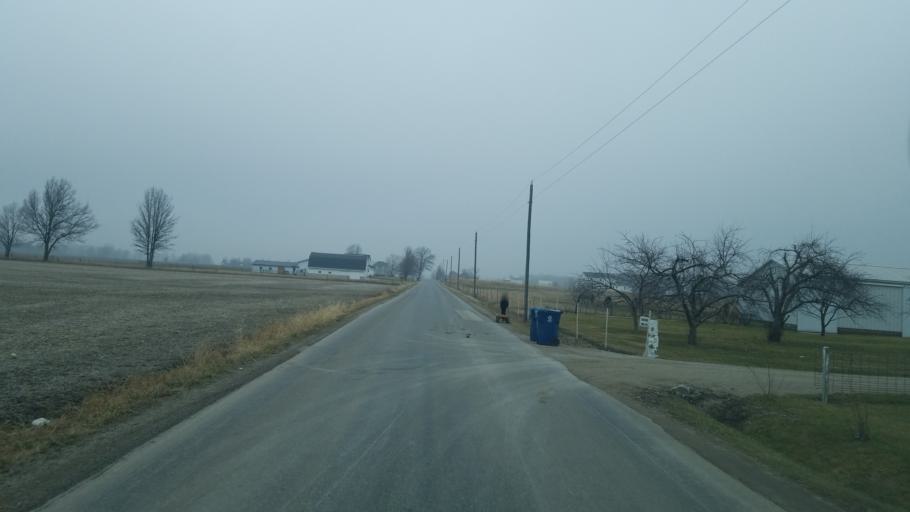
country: US
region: Indiana
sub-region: Adams County
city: Berne
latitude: 40.7197
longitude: -84.9751
